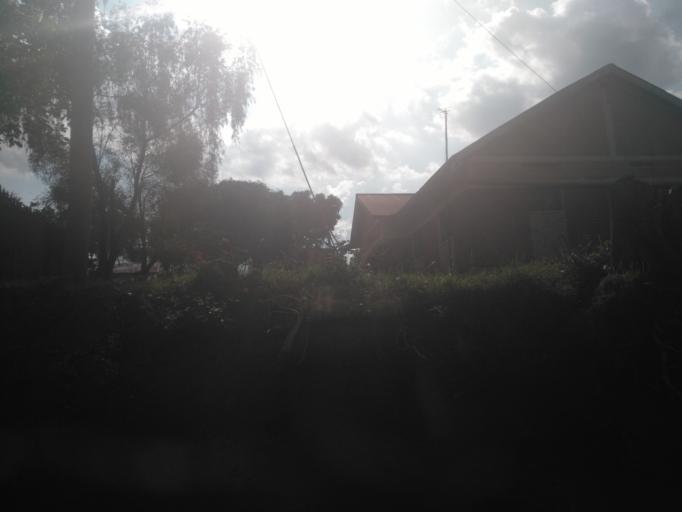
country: UG
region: Central Region
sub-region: Wakiso District
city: Kajansi
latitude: 0.2898
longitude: 32.4547
